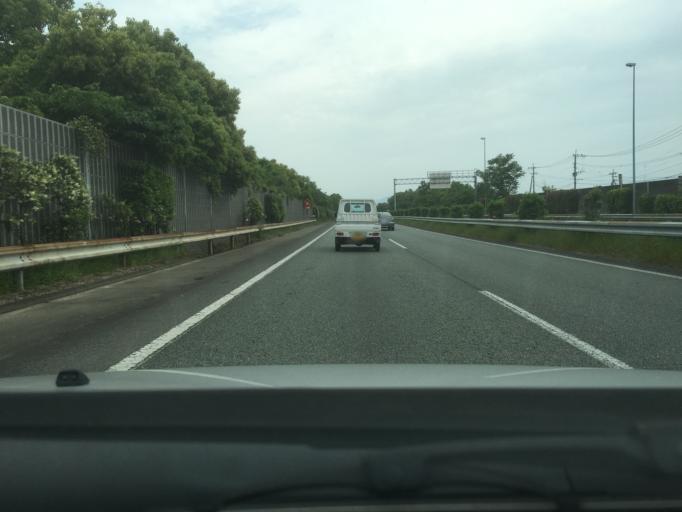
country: JP
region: Kumamoto
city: Ozu
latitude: 32.8327
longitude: 130.7806
